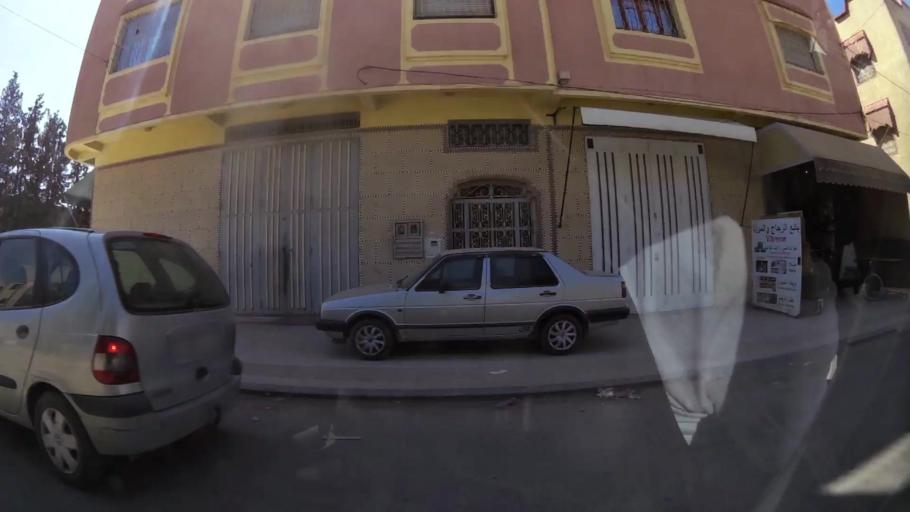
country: MA
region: Oriental
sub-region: Oujda-Angad
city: Oujda
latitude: 34.6868
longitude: -1.9377
